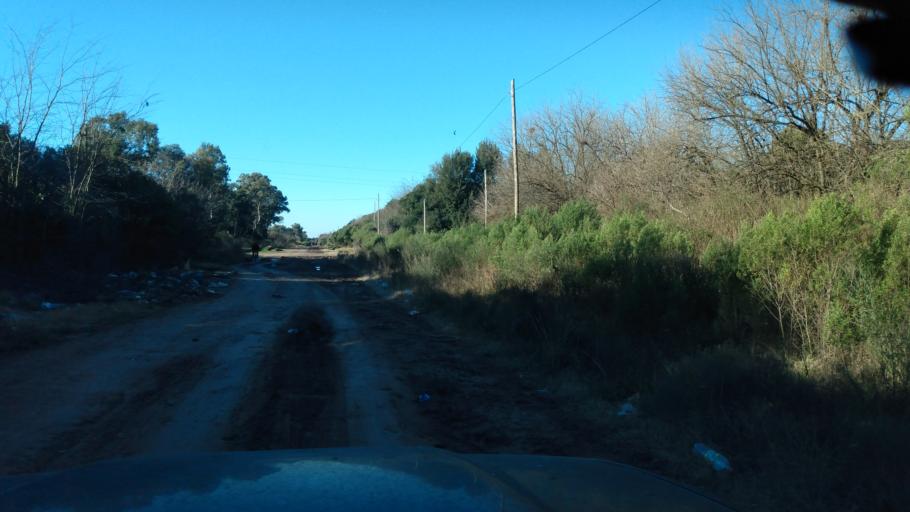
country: AR
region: Buenos Aires
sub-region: Partido de Lujan
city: Lujan
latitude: -34.5549
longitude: -59.1500
